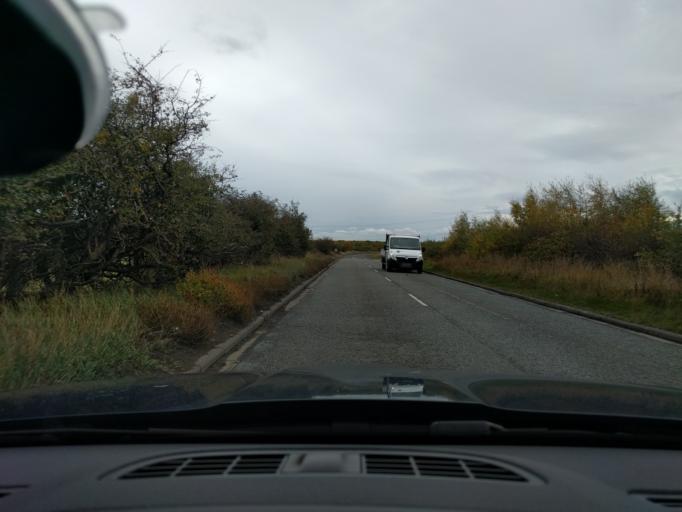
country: GB
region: England
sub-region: Northumberland
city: Ashington
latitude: 55.1521
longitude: -1.5517
